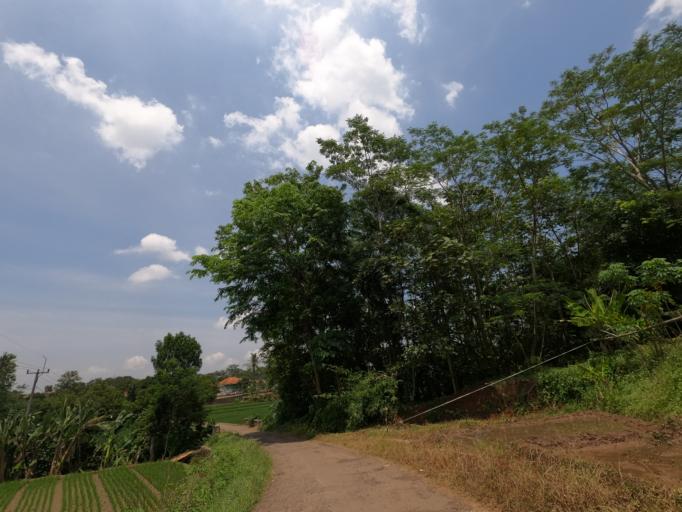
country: ID
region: West Java
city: Pamanukan
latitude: -6.5122
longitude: 107.7710
